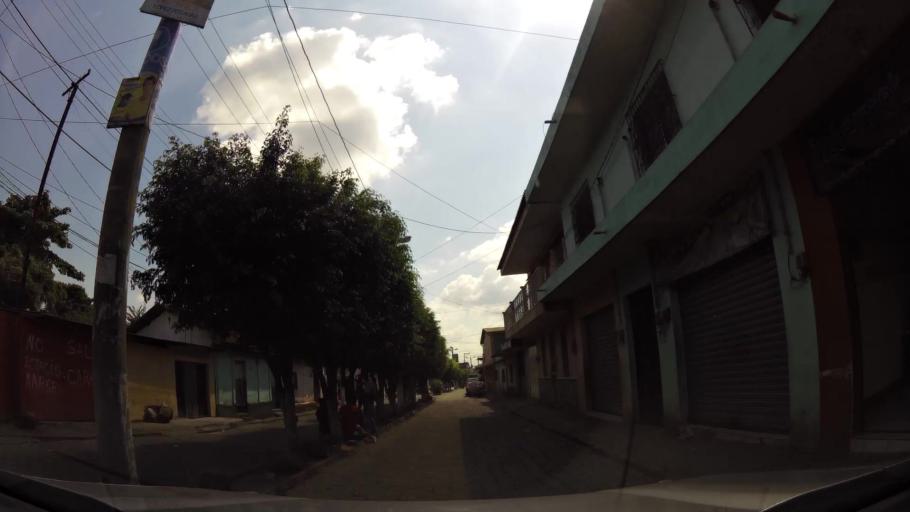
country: GT
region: Suchitepeque
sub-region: Municipio de Cuyotenango
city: Cuyotenango
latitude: 14.5433
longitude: -91.5711
